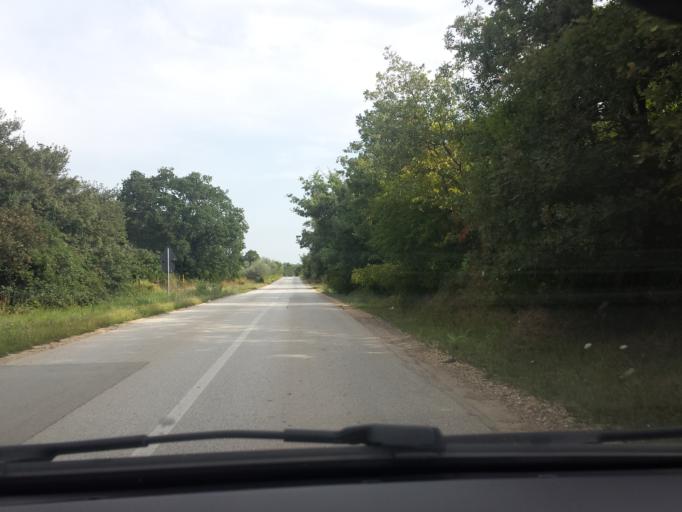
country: HR
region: Istarska
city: Galizana
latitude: 44.9136
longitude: 13.8583
